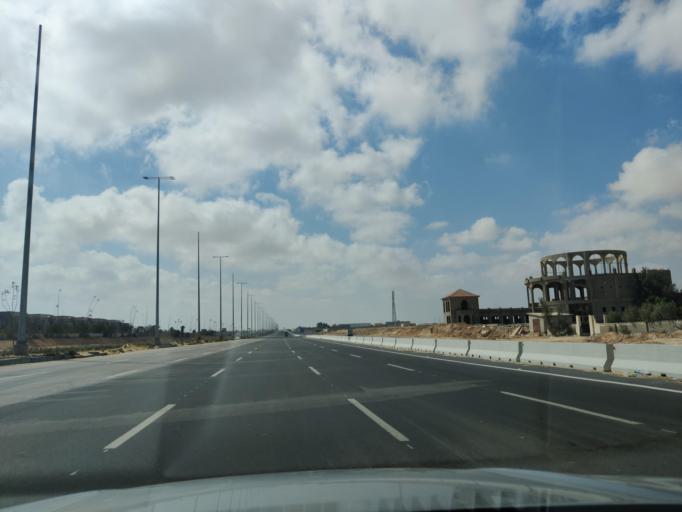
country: EG
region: Muhafazat Matruh
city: Al `Alamayn
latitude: 30.9392
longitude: 28.7841
